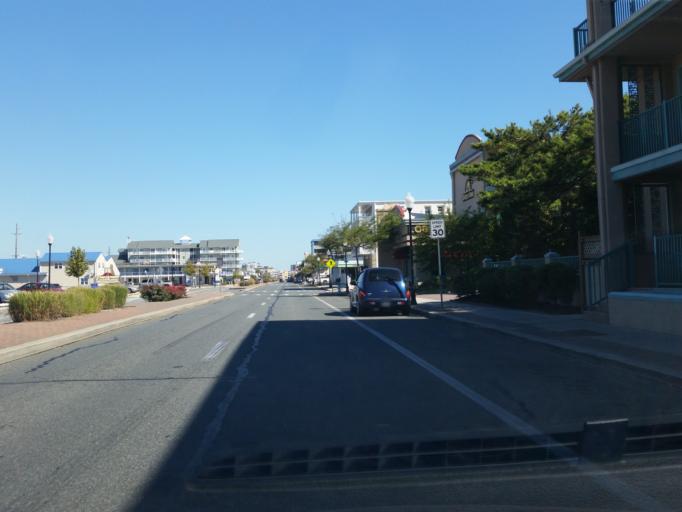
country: US
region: Maryland
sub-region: Worcester County
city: Ocean City
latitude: 38.3516
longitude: -75.0761
